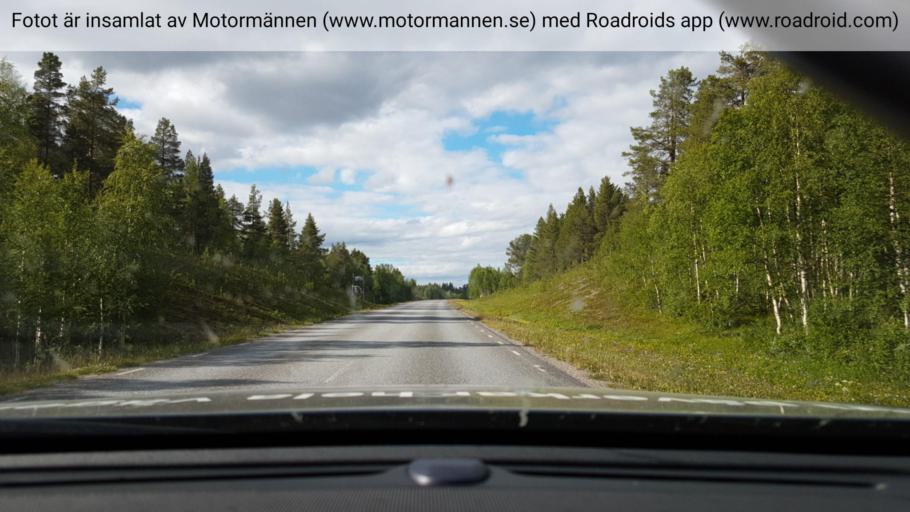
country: SE
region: Norrbotten
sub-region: Arjeplogs Kommun
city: Arjeplog
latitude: 66.2592
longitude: 17.1970
